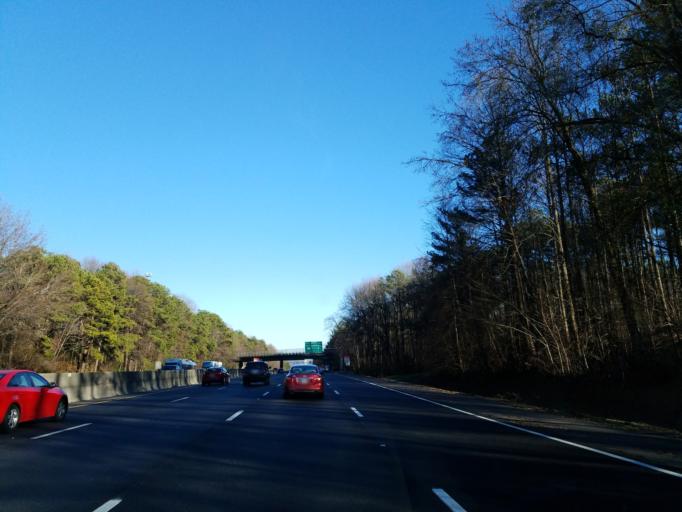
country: US
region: Georgia
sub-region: Cobb County
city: Mableton
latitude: 33.7752
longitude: -84.5816
